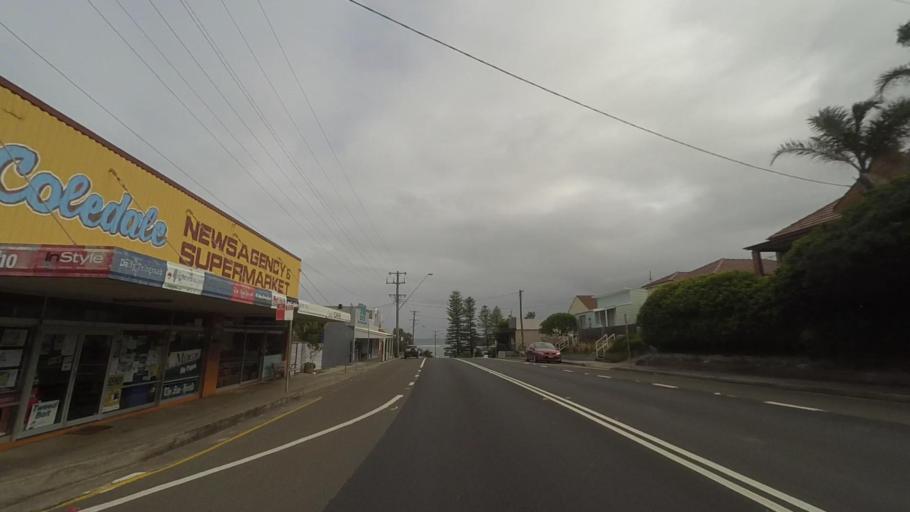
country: AU
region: New South Wales
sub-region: Wollongong
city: Bulli
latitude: -34.2918
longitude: 150.9444
